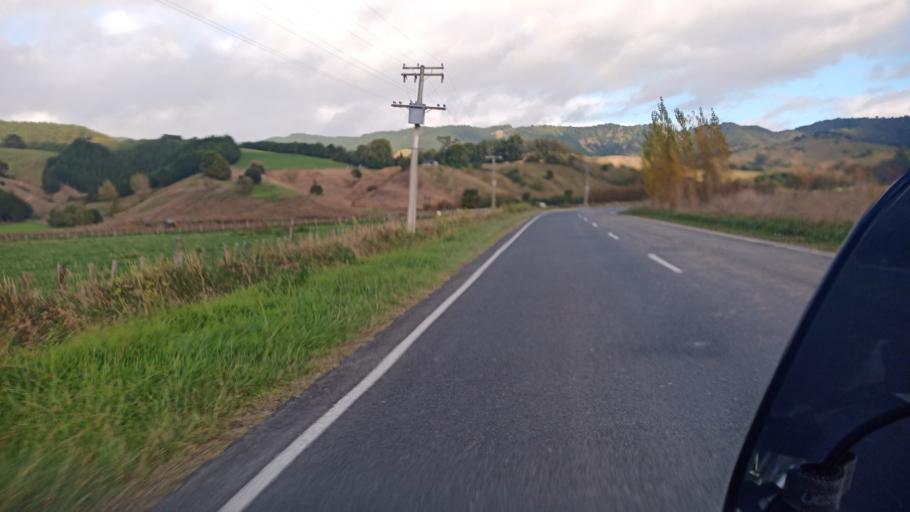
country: NZ
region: Gisborne
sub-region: Gisborne District
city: Gisborne
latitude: -38.6343
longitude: 177.8380
